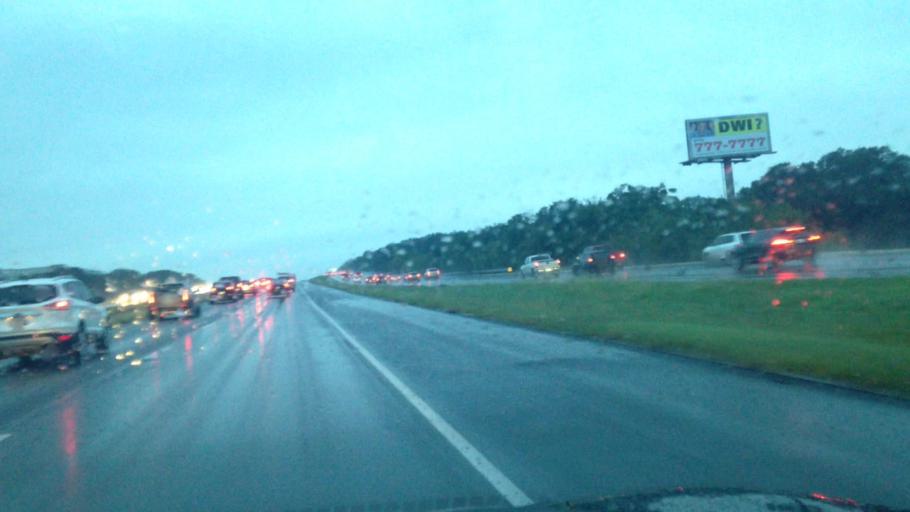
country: US
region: Texas
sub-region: Bexar County
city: Shavano Park
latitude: 29.6022
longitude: -98.5480
